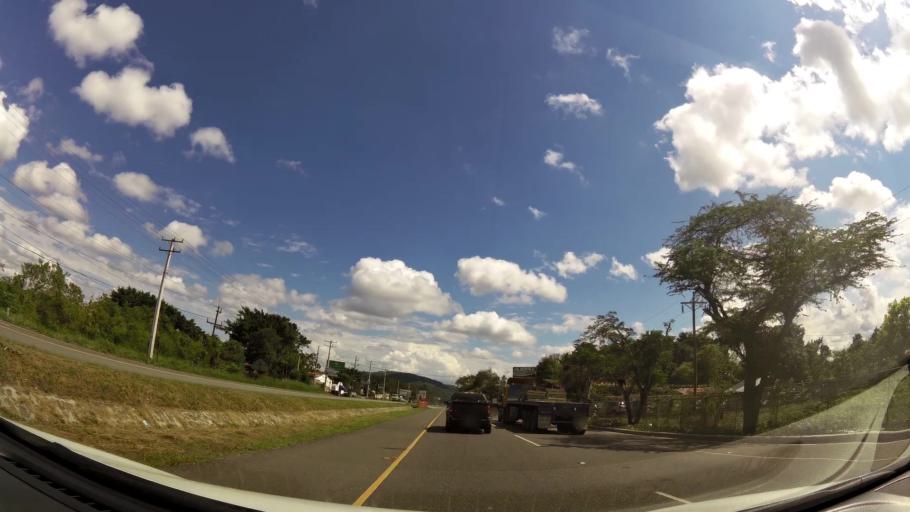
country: DO
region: La Vega
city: Rio Verde Arriba
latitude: 19.3324
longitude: -70.5944
